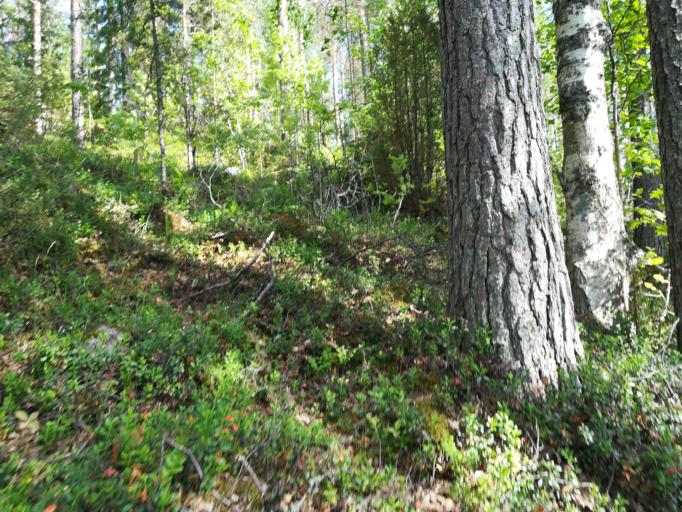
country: FI
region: South Karelia
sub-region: Imatra
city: Ruokolahti
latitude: 61.4807
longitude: 28.8692
